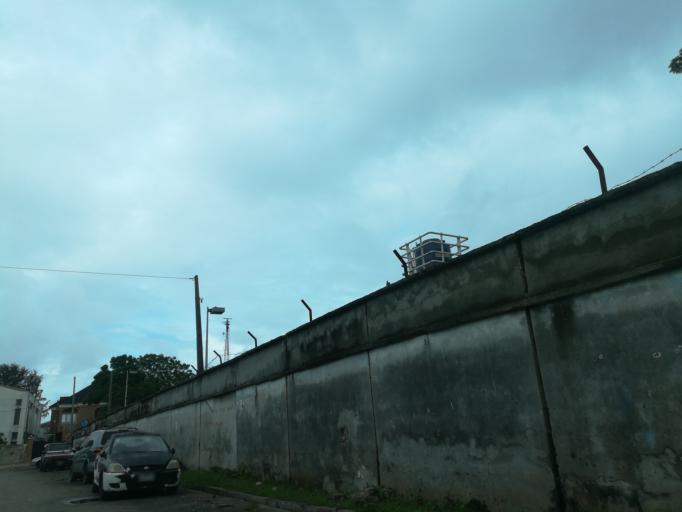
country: NG
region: Lagos
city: Lagos
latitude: 6.4223
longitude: 3.4095
